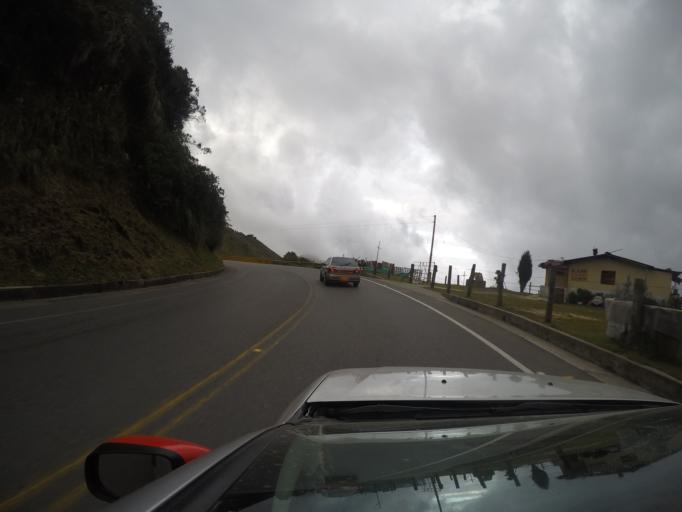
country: CO
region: Tolima
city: Herveo
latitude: 5.0664
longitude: -75.2914
